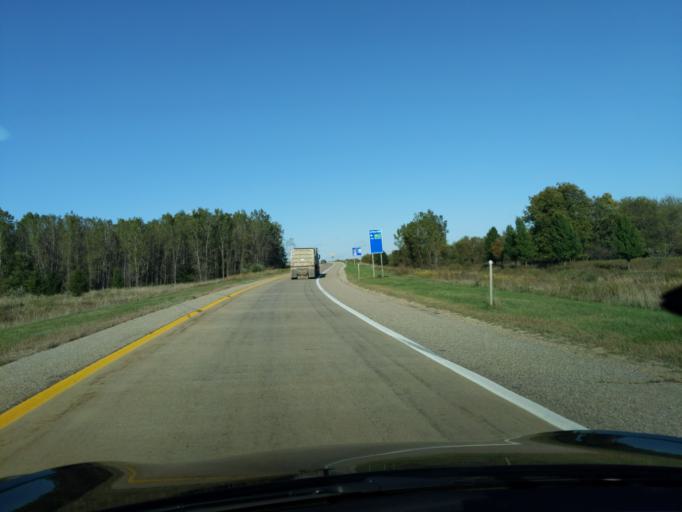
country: US
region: Michigan
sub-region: Clinton County
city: Saint Johns
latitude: 42.9249
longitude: -84.5176
